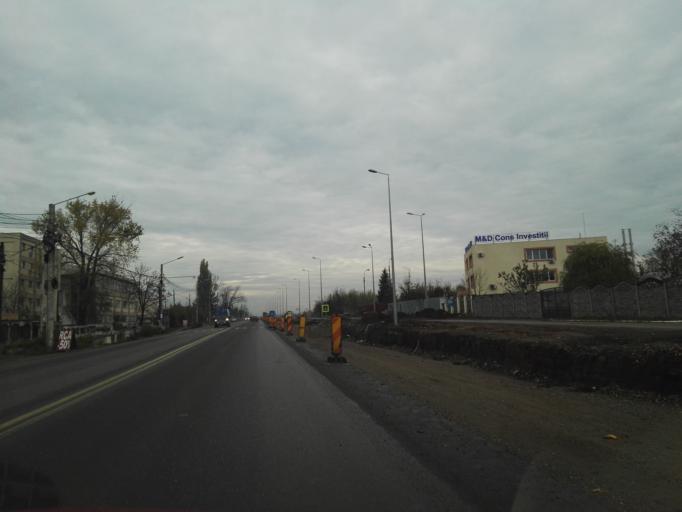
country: RO
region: Ilfov
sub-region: Comuna Jilava
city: Jilava
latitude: 44.3619
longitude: 26.0872
